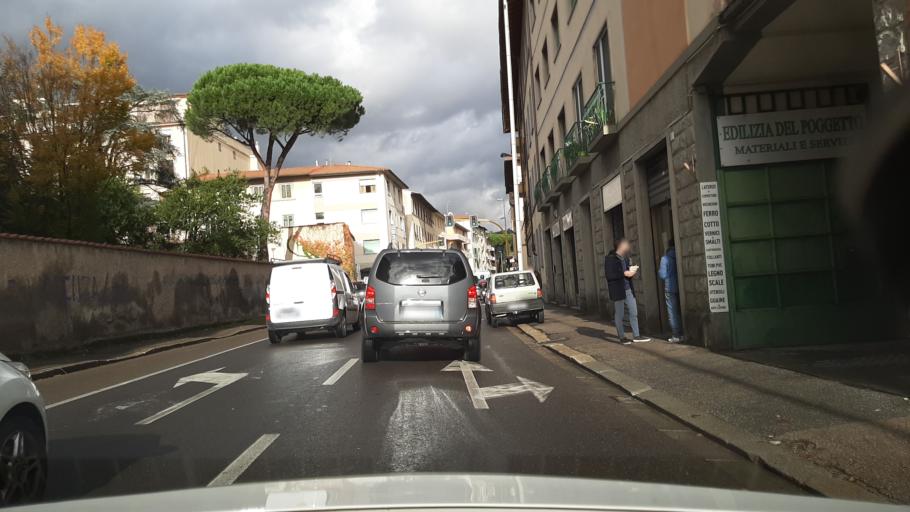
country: IT
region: Tuscany
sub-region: Province of Florence
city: Florence
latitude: 43.7971
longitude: 11.2448
